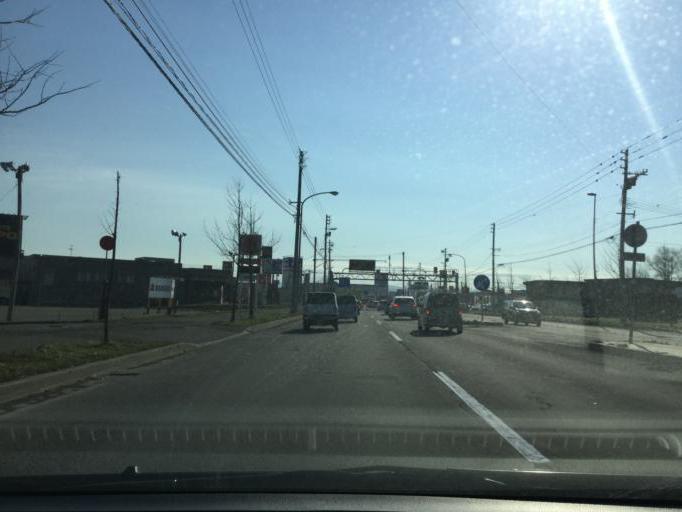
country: JP
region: Hokkaido
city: Iwamizawa
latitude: 43.1874
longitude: 141.7317
